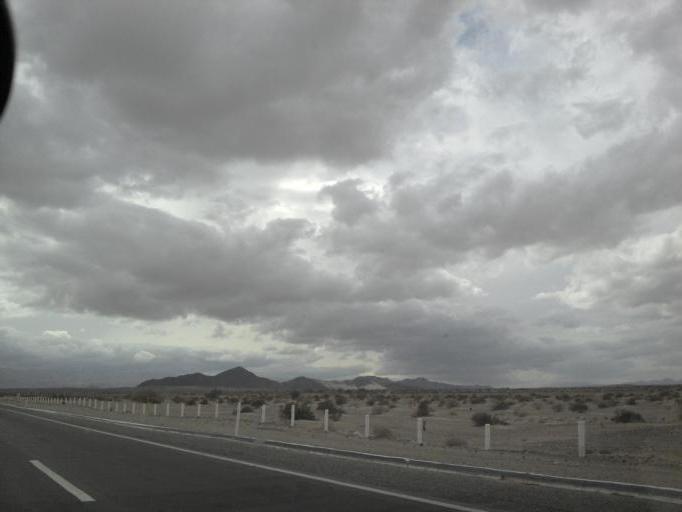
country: MX
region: Baja California
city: Progreso
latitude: 32.5716
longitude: -115.8017
